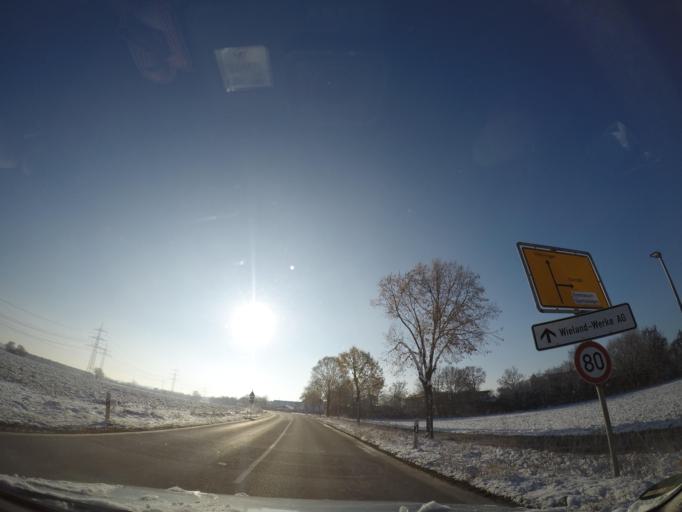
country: DE
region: Bavaria
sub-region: Swabia
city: Senden
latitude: 48.3037
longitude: 10.0550
